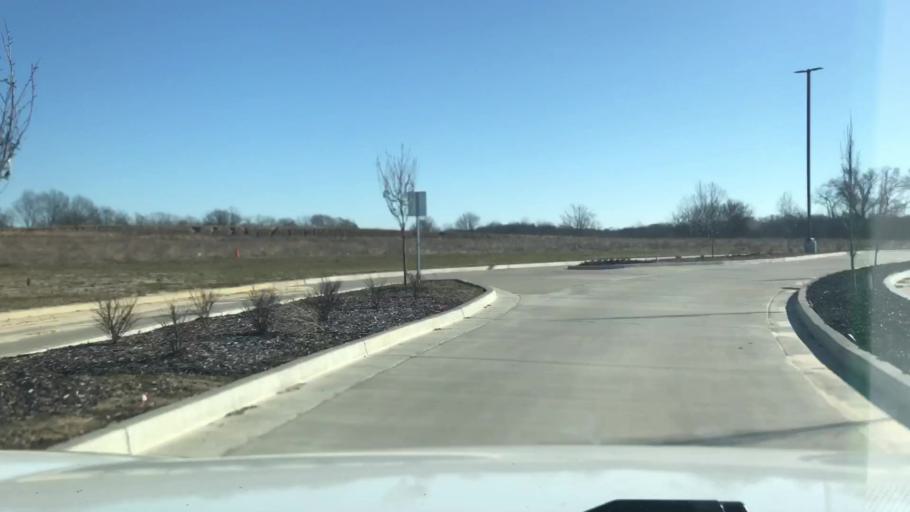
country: US
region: Illinois
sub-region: Saint Clair County
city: Alorton
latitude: 38.5638
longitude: -90.0832
